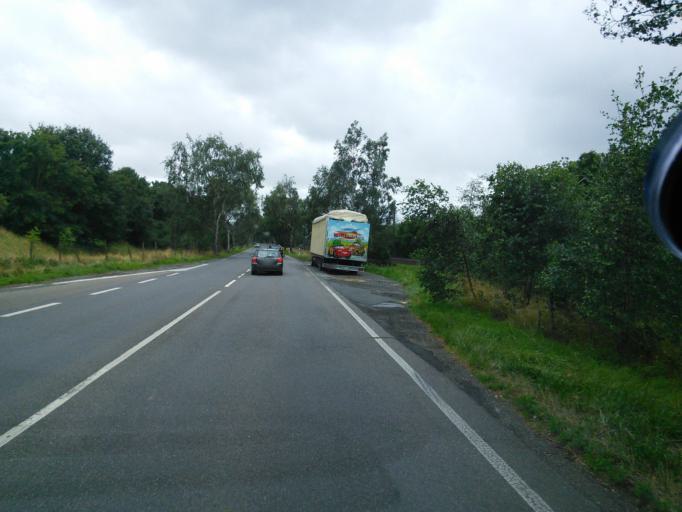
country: DE
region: North Rhine-Westphalia
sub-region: Regierungsbezirk Koln
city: Bonn
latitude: 50.7519
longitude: 7.1388
